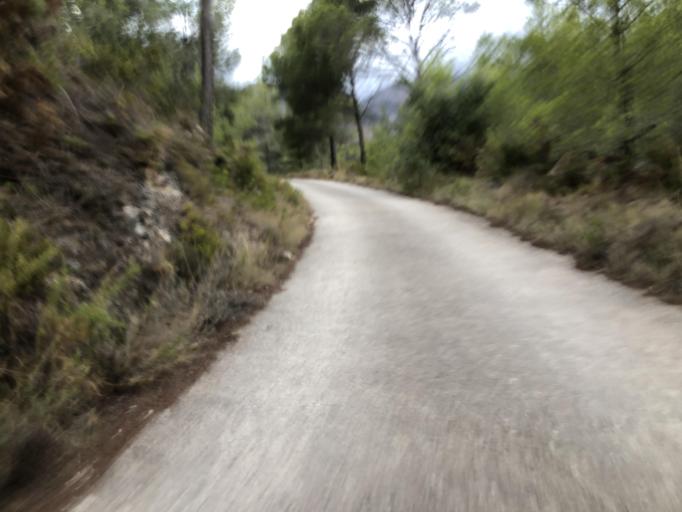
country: ES
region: Valencia
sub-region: Provincia de Alicante
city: Polop
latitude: 38.6388
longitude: -0.1393
